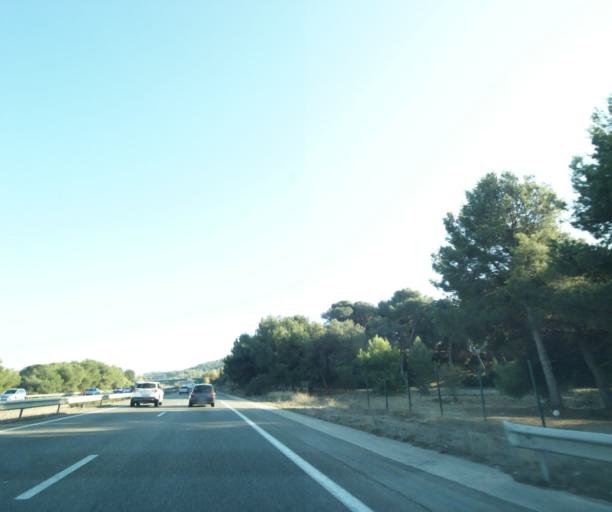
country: FR
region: Provence-Alpes-Cote d'Azur
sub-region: Departement des Bouches-du-Rhone
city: Chateauneuf-les-Martigues
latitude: 43.3976
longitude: 5.1218
